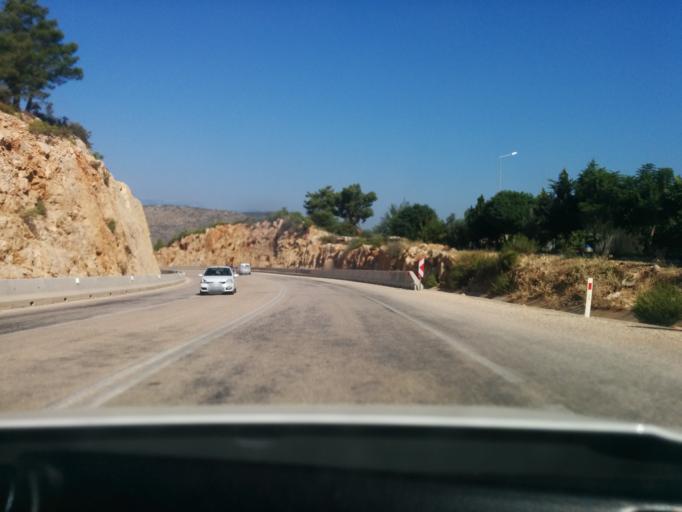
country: TR
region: Antalya
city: Kalkan
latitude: 36.2742
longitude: 29.3944
